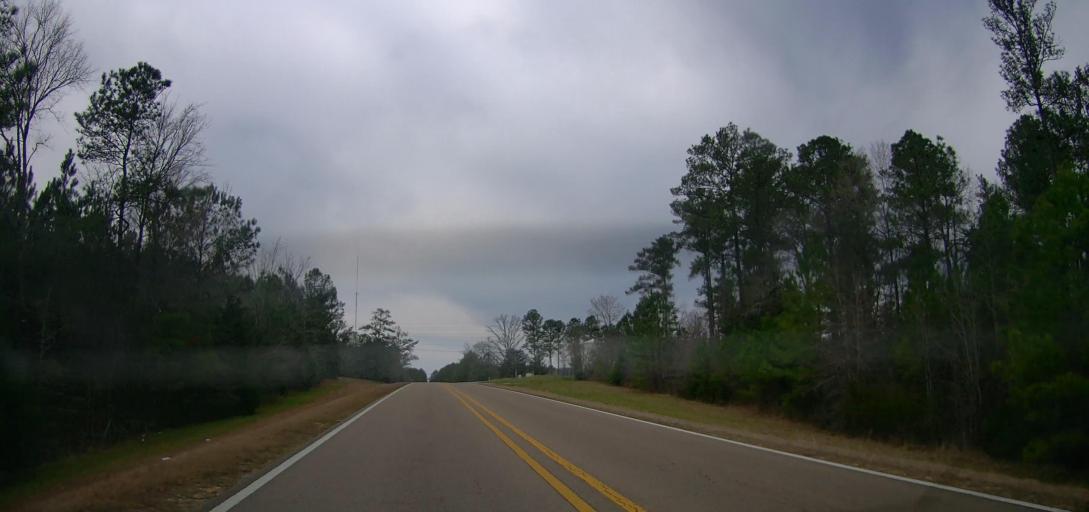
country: US
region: Mississippi
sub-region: Itawamba County
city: Mantachie
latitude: 34.2621
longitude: -88.5298
